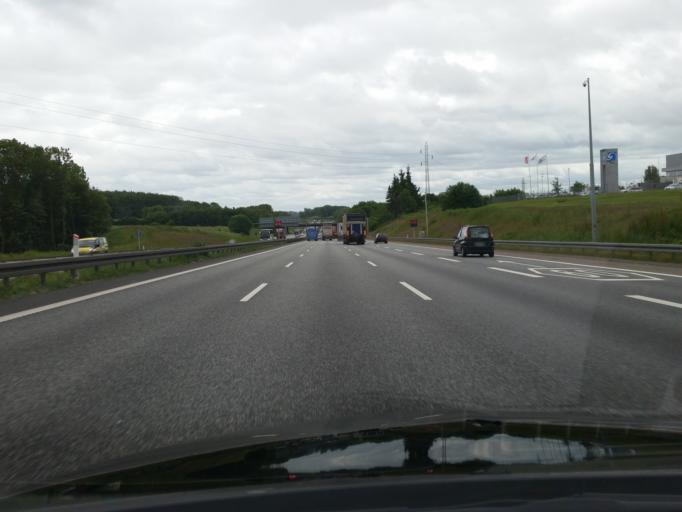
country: DK
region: South Denmark
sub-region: Vejle Kommune
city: Vejle
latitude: 55.7299
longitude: 9.5760
